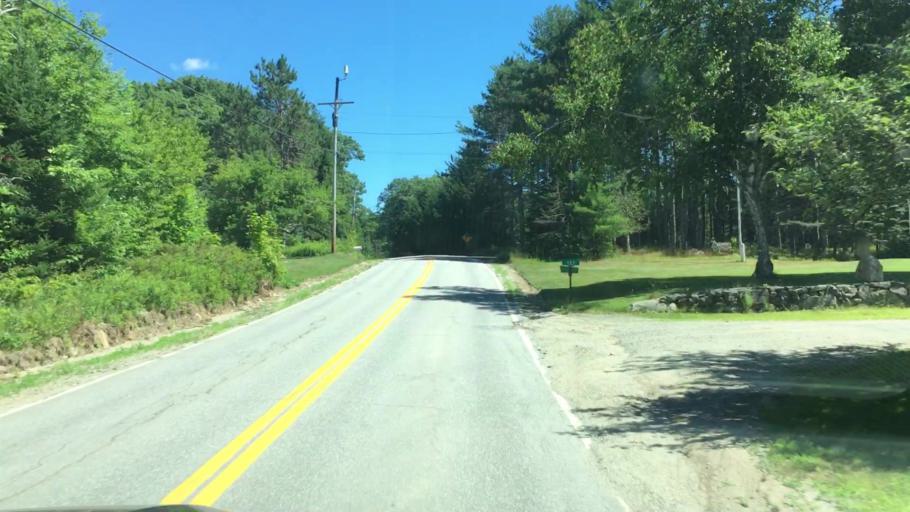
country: US
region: Maine
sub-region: Hancock County
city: Penobscot
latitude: 44.4359
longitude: -68.7128
